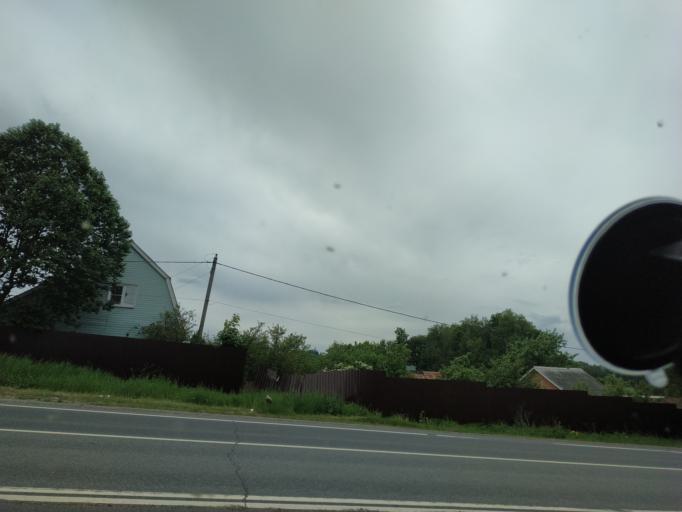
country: RU
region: Moskovskaya
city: Ostrovtsy
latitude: 55.5508
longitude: 38.0623
